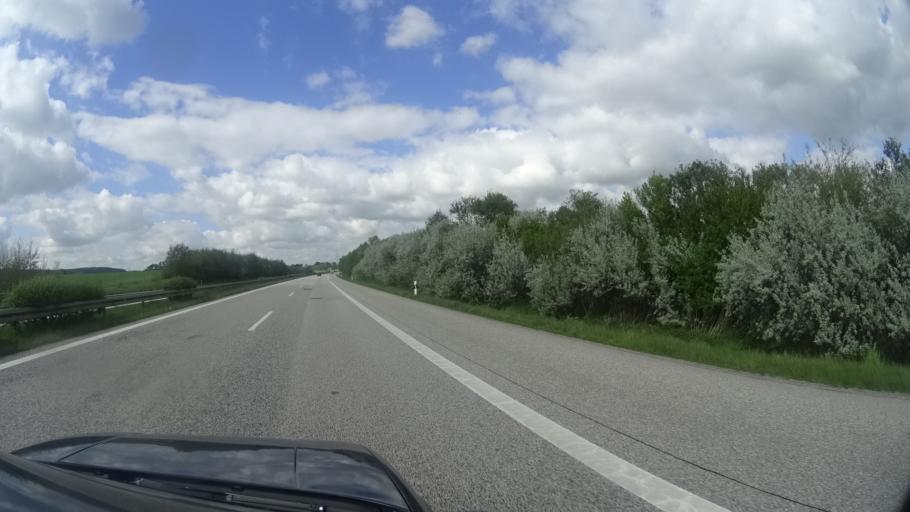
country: DE
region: Mecklenburg-Vorpommern
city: Muhl Rosin
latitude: 53.8057
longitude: 12.2980
